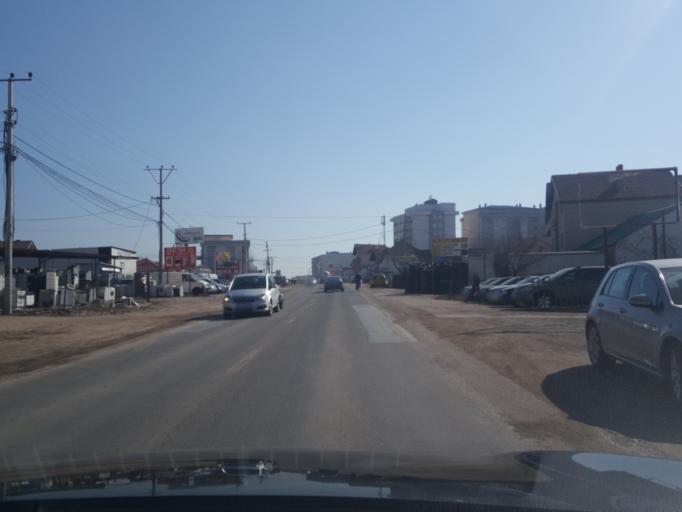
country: XK
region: Mitrovica
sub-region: Vushtrri
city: Vushtrri
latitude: 42.8296
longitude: 20.9661
